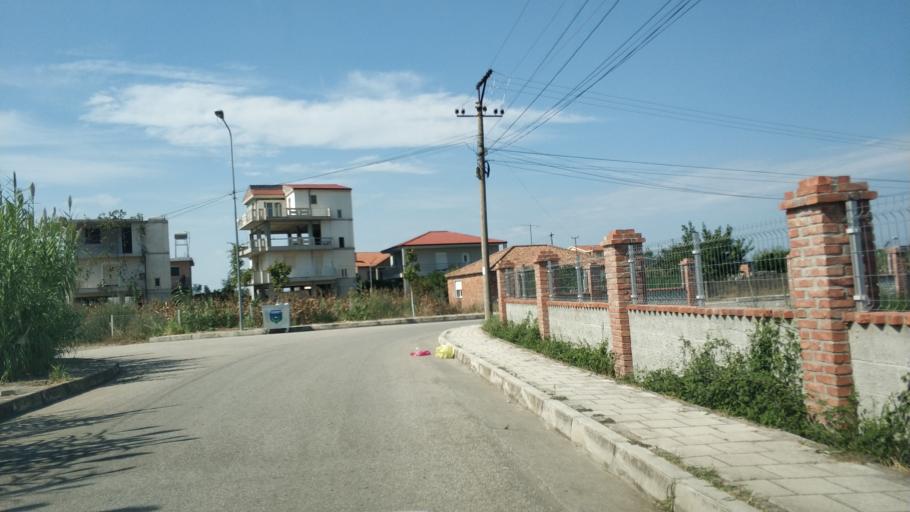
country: AL
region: Fier
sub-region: Rrethi i Lushnjes
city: Divjake
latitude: 40.9989
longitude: 19.5258
